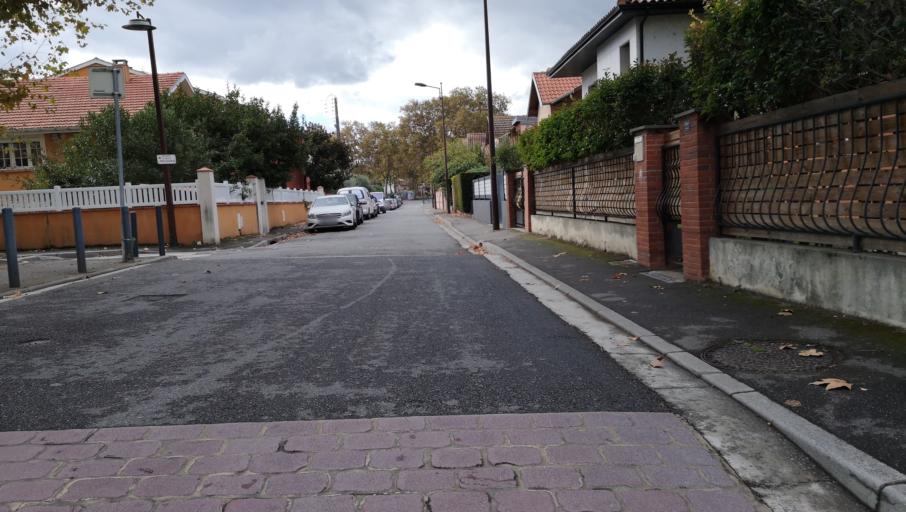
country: FR
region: Midi-Pyrenees
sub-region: Departement de la Haute-Garonne
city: Toulouse
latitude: 43.6057
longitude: 1.4118
